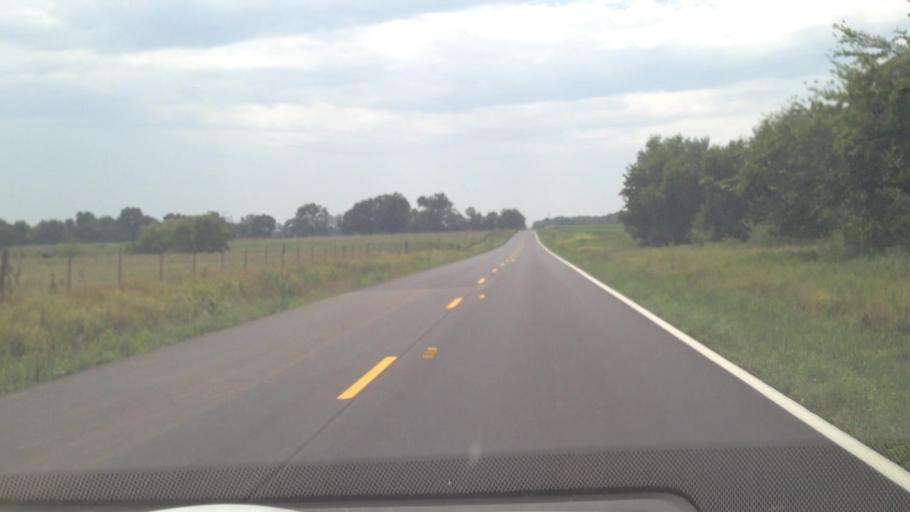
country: US
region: Kansas
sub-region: Crawford County
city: Girard
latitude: 37.5335
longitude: -94.9606
